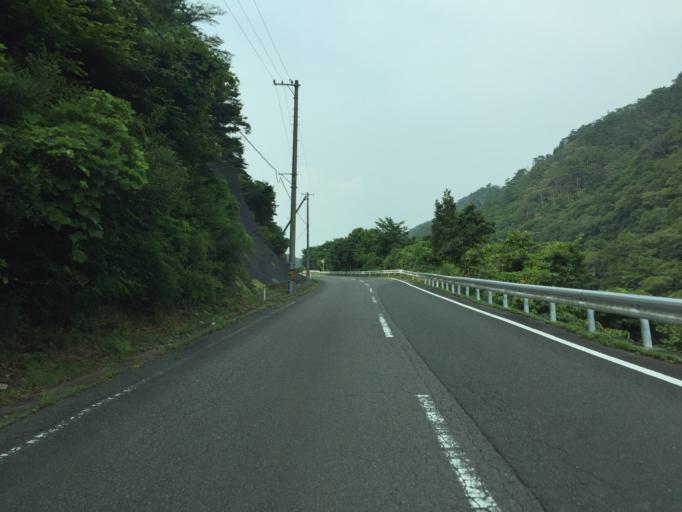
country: JP
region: Fukushima
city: Namie
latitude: 37.5817
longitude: 140.8866
